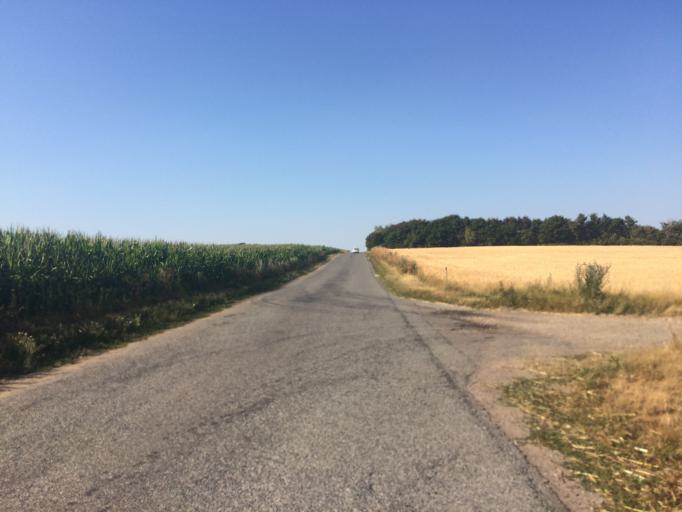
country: DK
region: Central Jutland
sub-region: Holstebro Kommune
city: Vinderup
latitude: 56.5903
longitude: 8.7379
